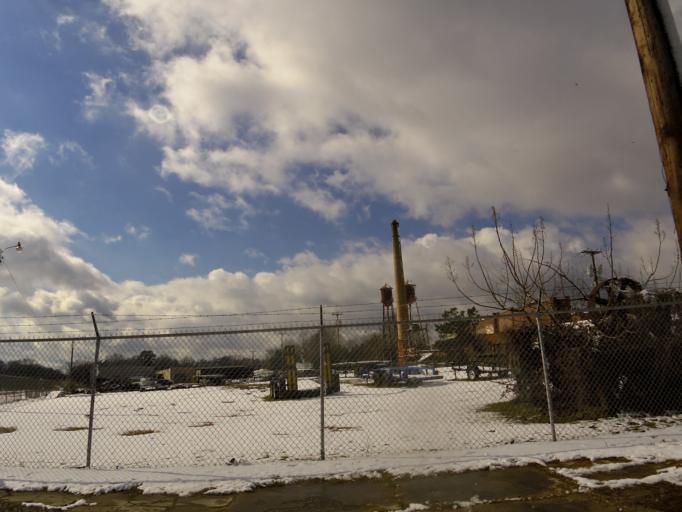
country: US
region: North Carolina
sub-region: Wilson County
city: Wilson
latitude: 35.7215
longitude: -77.9089
